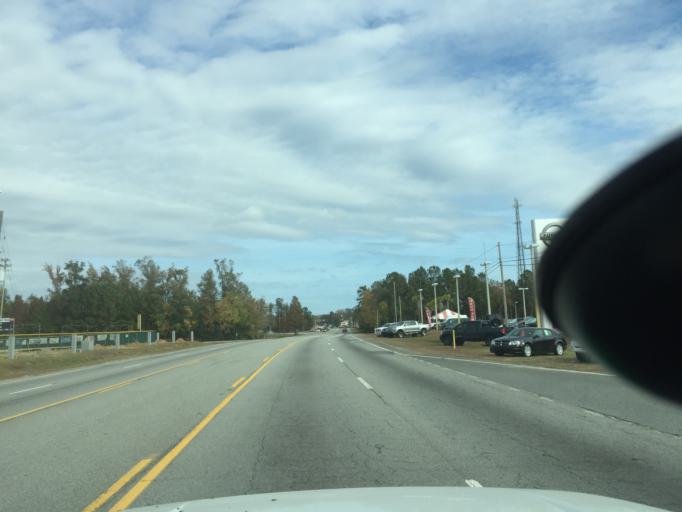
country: US
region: Georgia
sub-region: Chatham County
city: Garden City
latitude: 32.0749
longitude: -81.1598
